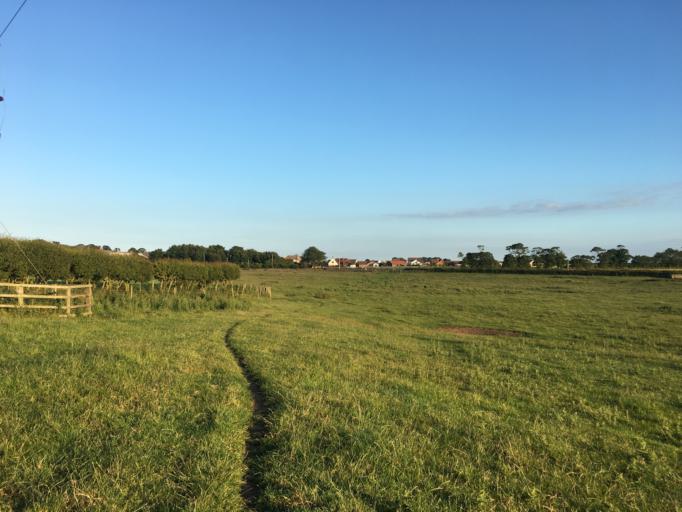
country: GB
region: England
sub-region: Northumberland
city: North Sunderland
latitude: 55.5807
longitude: -1.6715
